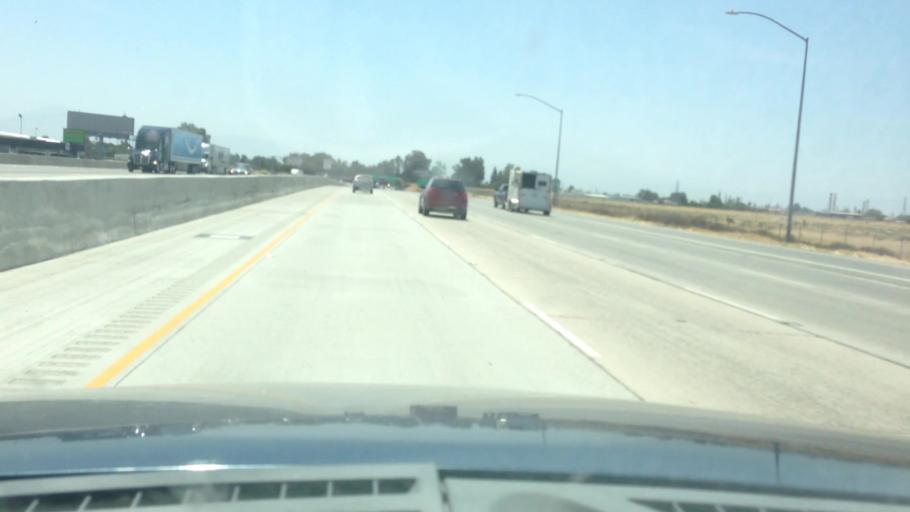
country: US
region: California
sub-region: Kern County
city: Oildale
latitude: 35.4103
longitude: -119.0528
